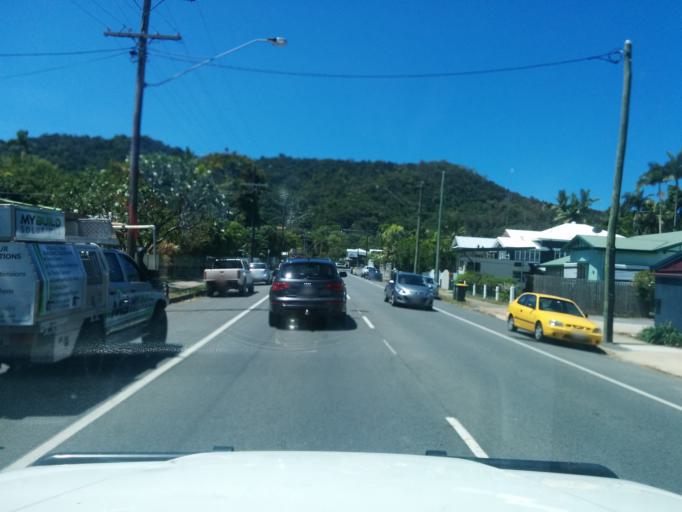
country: AU
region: Queensland
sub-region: Cairns
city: Cairns
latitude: -16.9028
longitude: 145.7420
